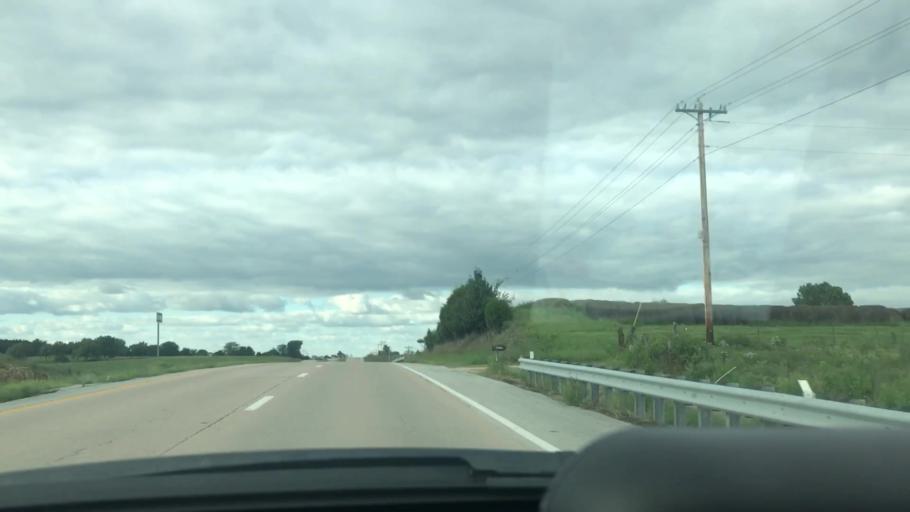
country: US
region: Missouri
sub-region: Benton County
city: Lincoln
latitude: 38.3225
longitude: -93.3420
